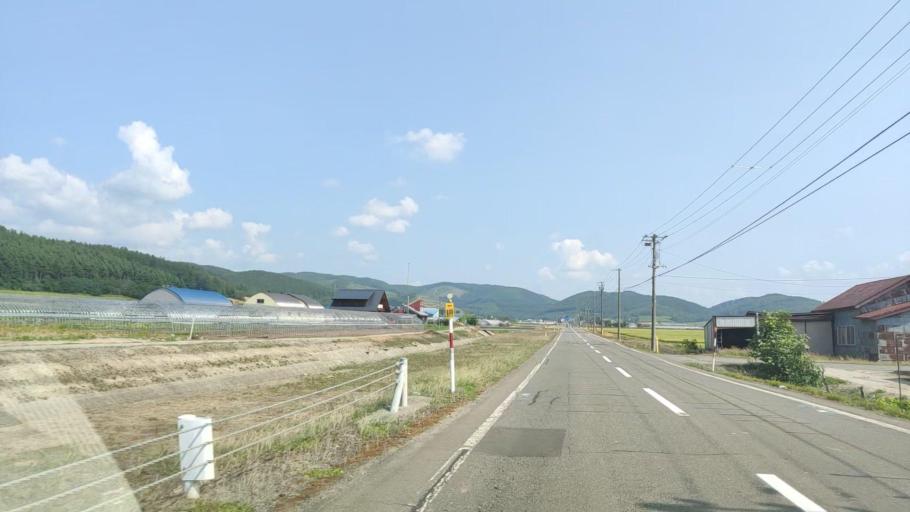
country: JP
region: Hokkaido
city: Shimo-furano
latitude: 43.3982
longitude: 142.3926
